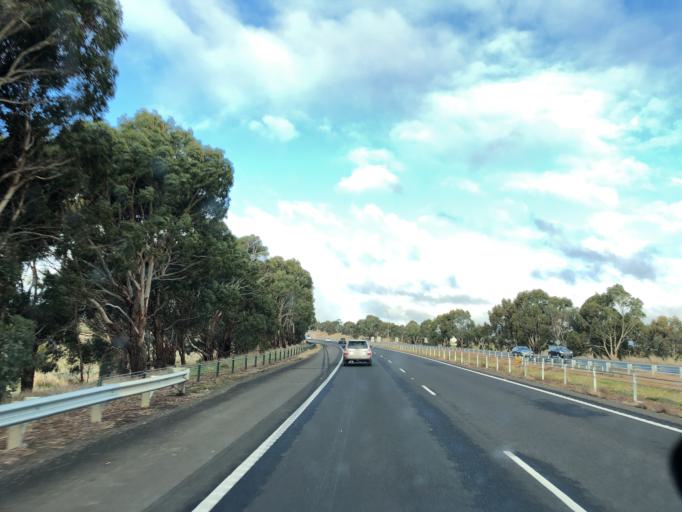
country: AU
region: Victoria
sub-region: Mount Alexander
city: Castlemaine
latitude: -37.2227
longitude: 144.4199
